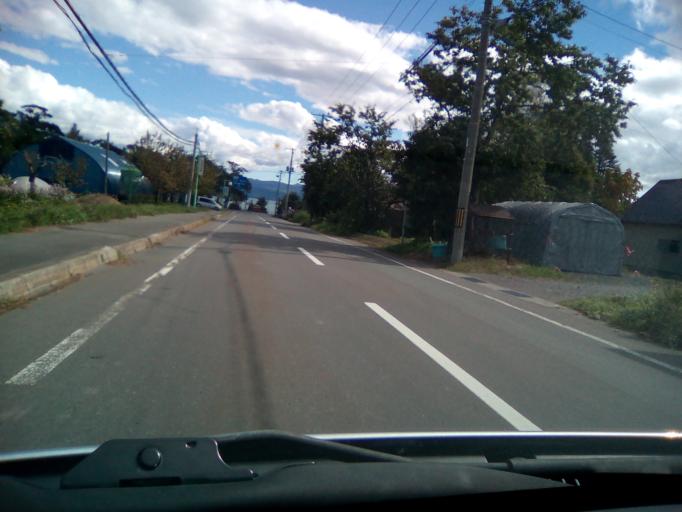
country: JP
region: Hokkaido
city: Date
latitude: 42.6457
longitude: 140.8282
